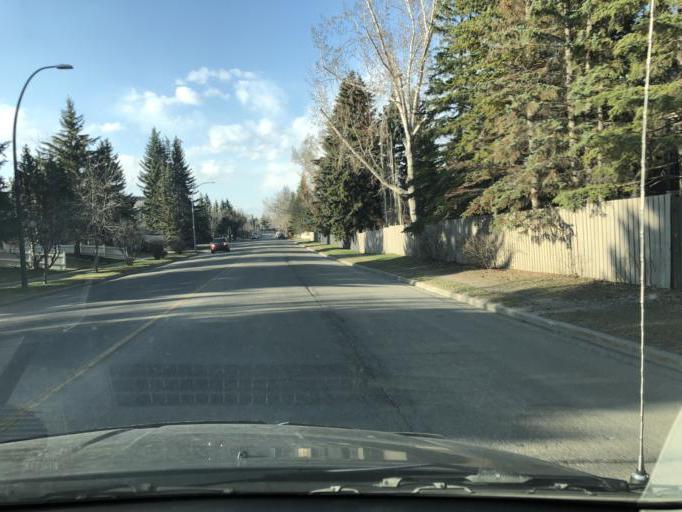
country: CA
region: Alberta
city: Calgary
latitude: 50.9678
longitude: -114.1063
